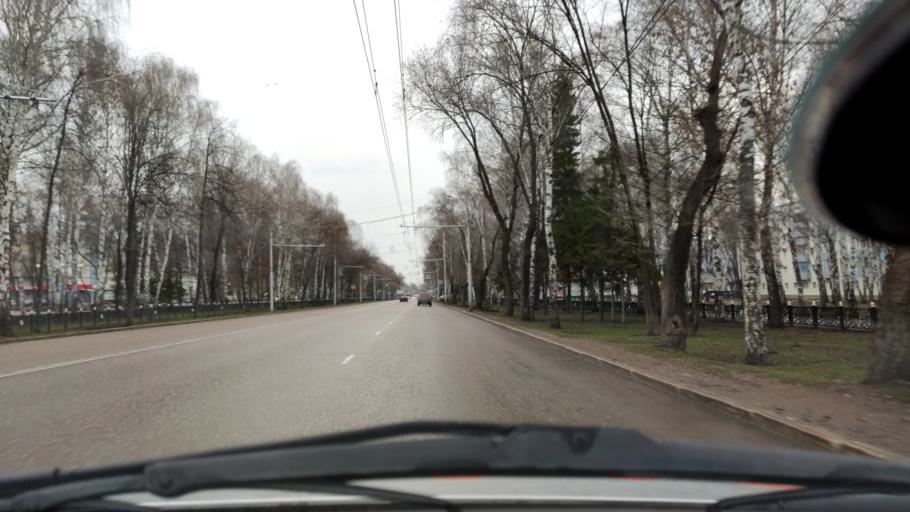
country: RU
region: Bashkortostan
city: Sterlitamak
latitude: 53.6326
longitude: 55.9331
